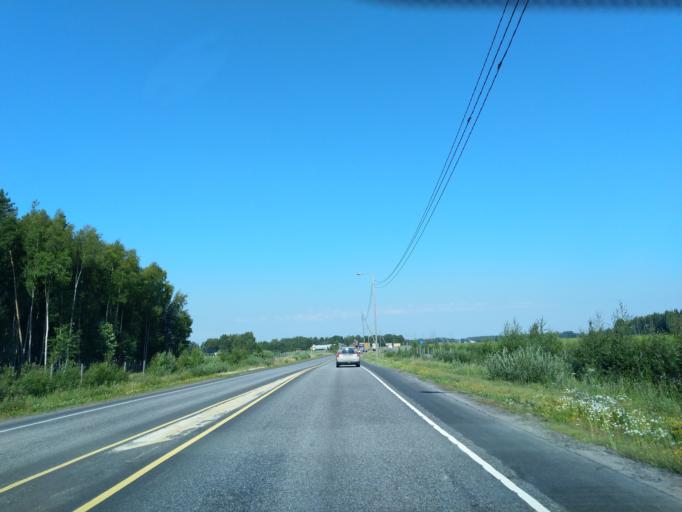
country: FI
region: Satakunta
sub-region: Pori
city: Nakkila
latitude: 61.3454
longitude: 22.0234
